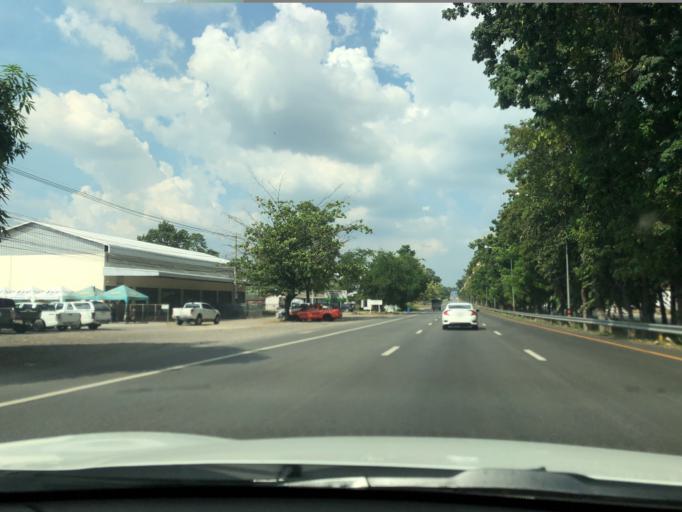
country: TH
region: Nakhon Sawan
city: Nakhon Sawan
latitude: 15.6331
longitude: 100.1290
